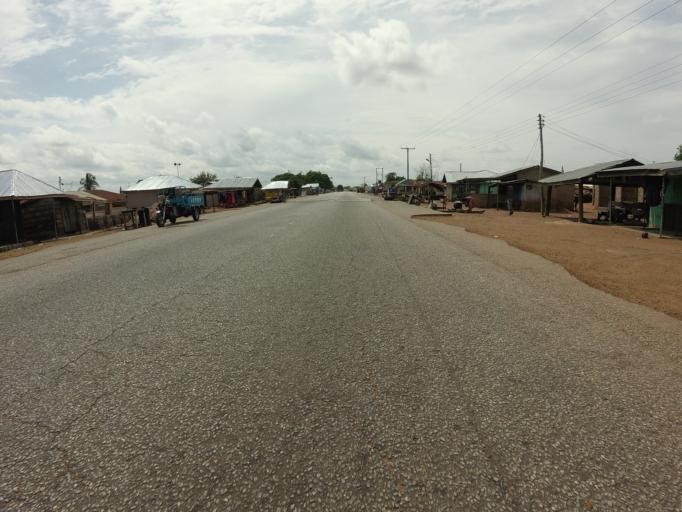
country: GH
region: Brong-Ahafo
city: Kintampo
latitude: 8.4487
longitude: -1.5651
